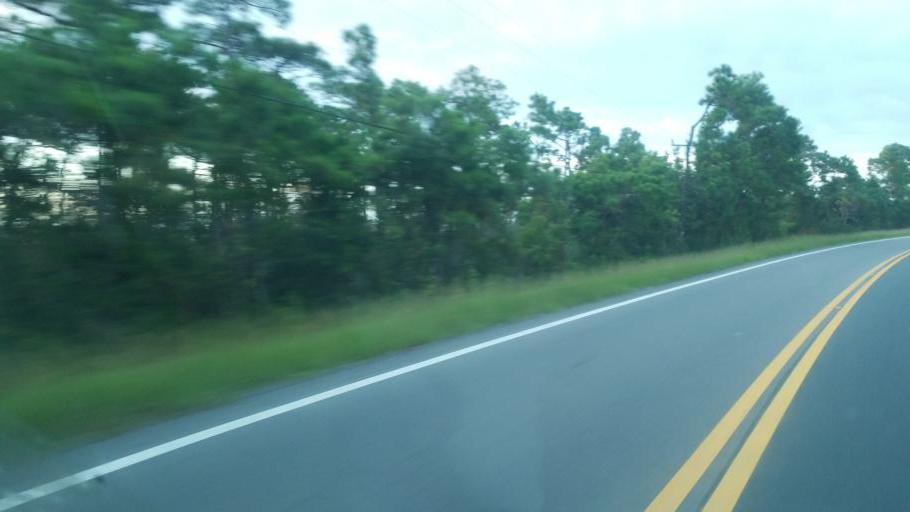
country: US
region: North Carolina
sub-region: Dare County
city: Wanchese
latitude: 35.8757
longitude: -75.6535
